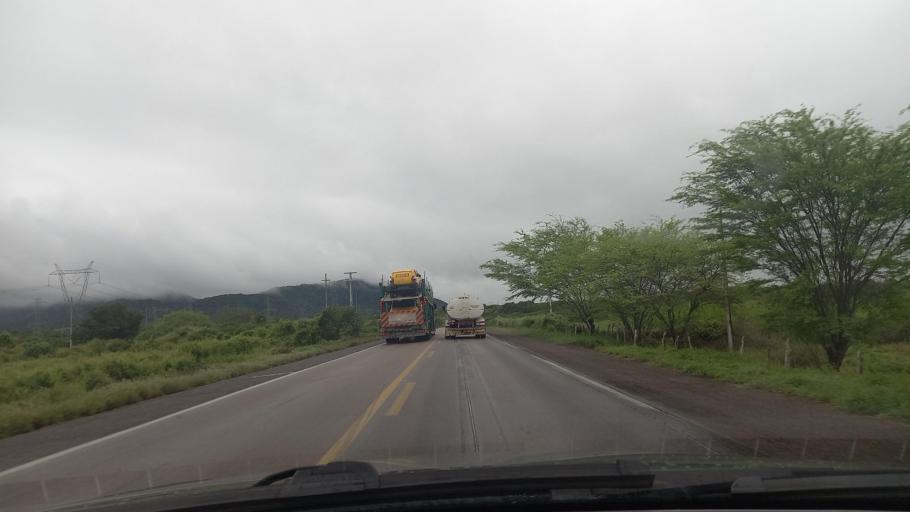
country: BR
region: Alagoas
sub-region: Agua Branca
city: Agua Branca
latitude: -9.3239
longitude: -37.9658
